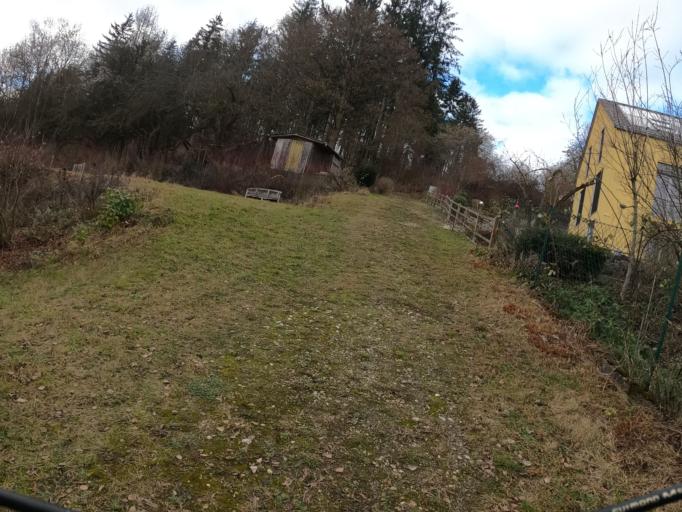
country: DE
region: Bavaria
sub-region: Swabia
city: Nersingen
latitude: 48.4526
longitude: 10.0954
